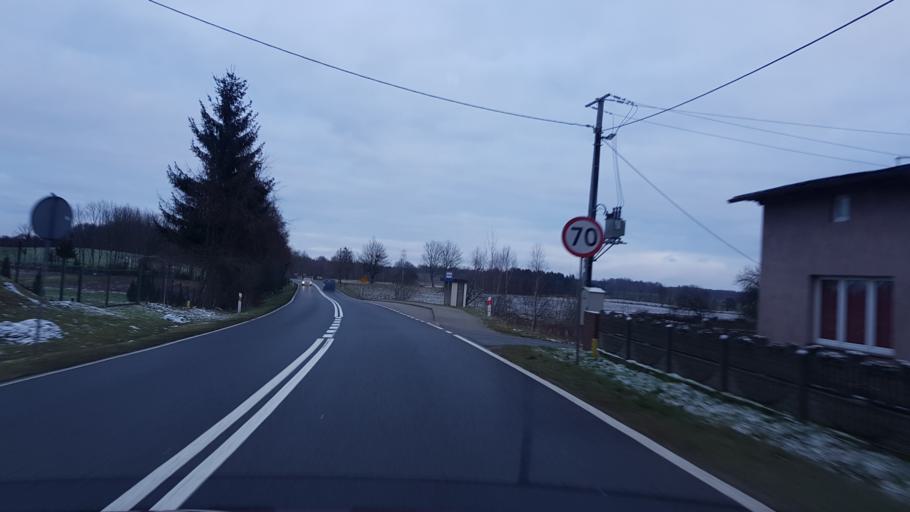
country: PL
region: Pomeranian Voivodeship
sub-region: Powiat czluchowski
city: Koczala
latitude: 54.0102
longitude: 17.0990
